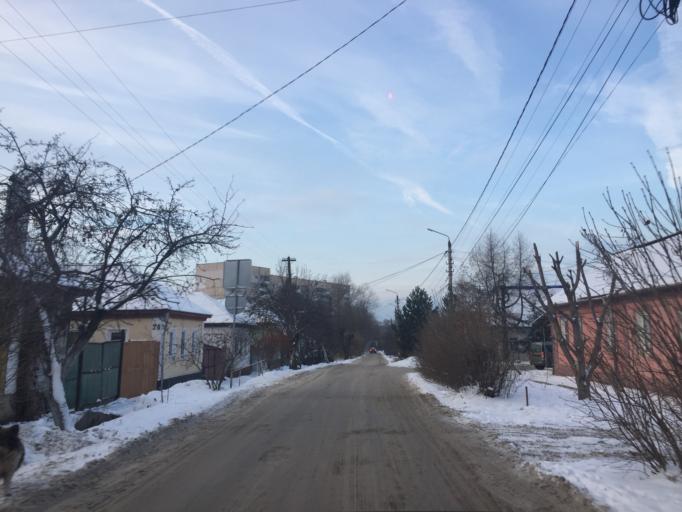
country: RU
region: Tula
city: Tula
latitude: 54.1971
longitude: 37.6803
